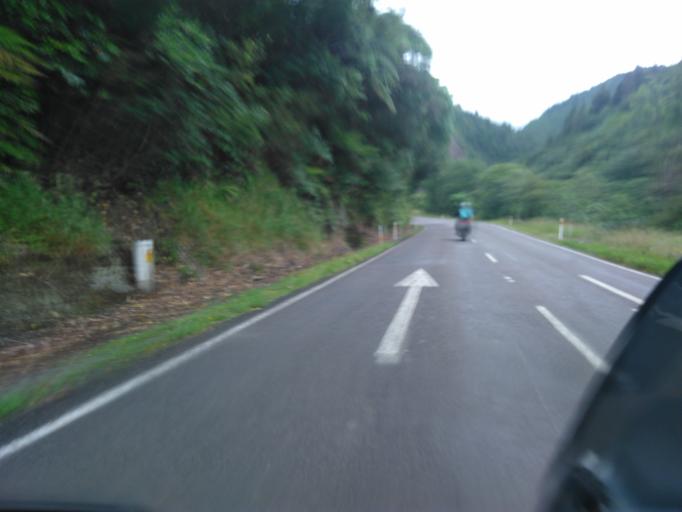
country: NZ
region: Bay of Plenty
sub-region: Opotiki District
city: Opotiki
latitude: -38.3038
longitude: 177.3960
